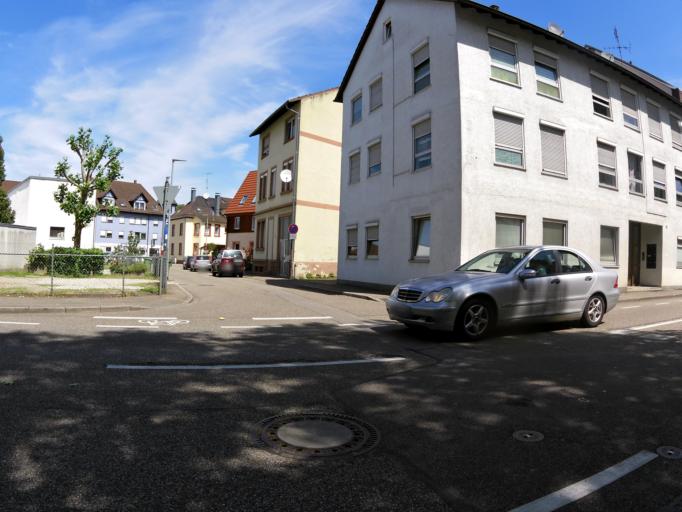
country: DE
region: Baden-Wuerttemberg
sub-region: Freiburg Region
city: Lahr
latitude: 48.3401
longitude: 7.8769
